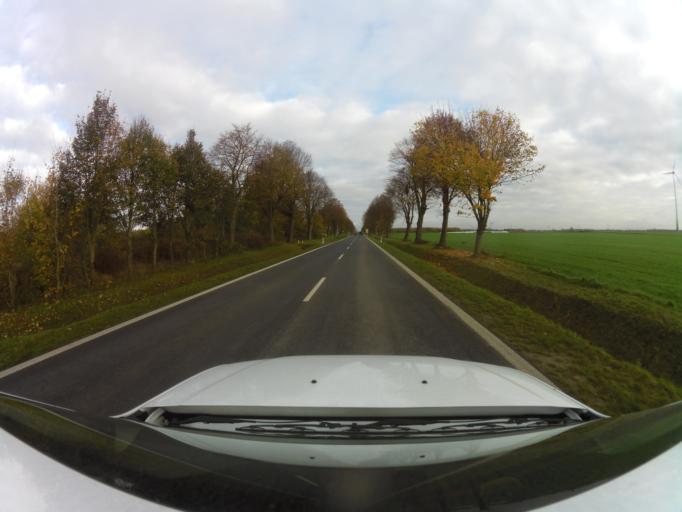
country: PL
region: West Pomeranian Voivodeship
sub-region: Powiat gryficki
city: Trzebiatow
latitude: 54.0405
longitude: 15.2482
